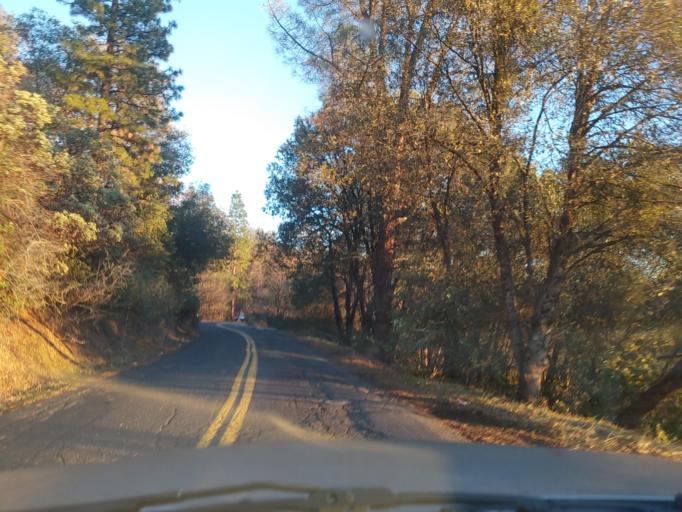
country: US
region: California
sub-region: Tuolumne County
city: Cedar Ridge
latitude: 38.0404
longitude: -120.2792
